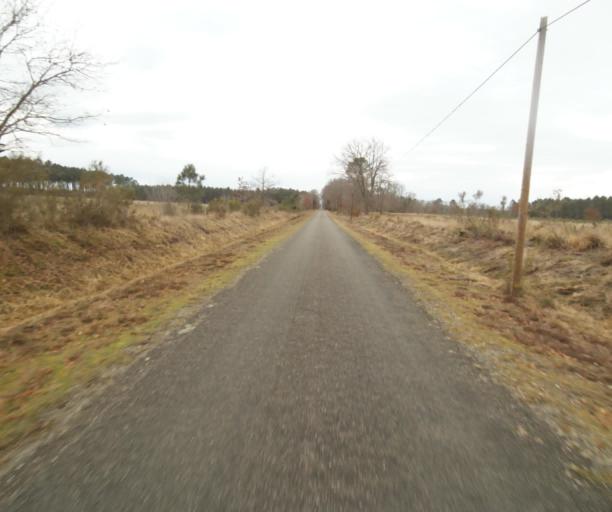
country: FR
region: Aquitaine
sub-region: Departement des Landes
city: Gabarret
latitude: 44.0424
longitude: -0.0806
